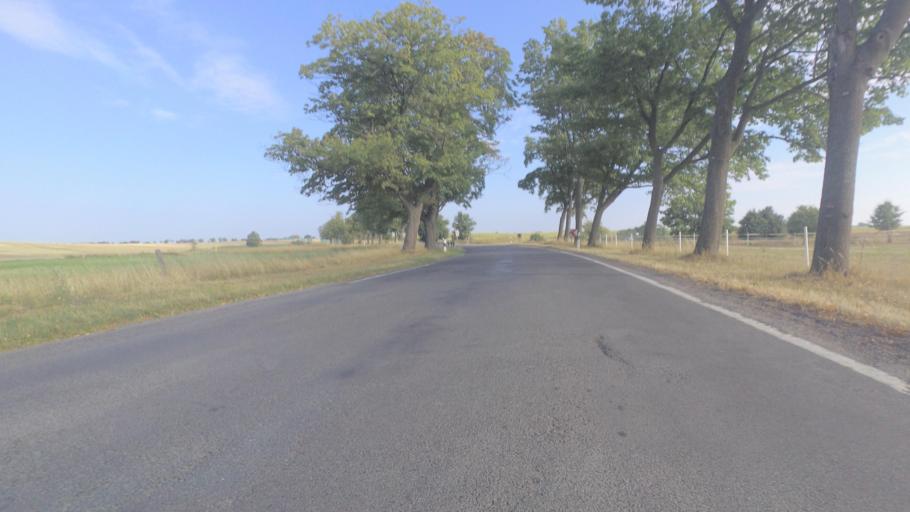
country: DE
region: Brandenburg
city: Kremmen
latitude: 52.7397
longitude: 12.9539
